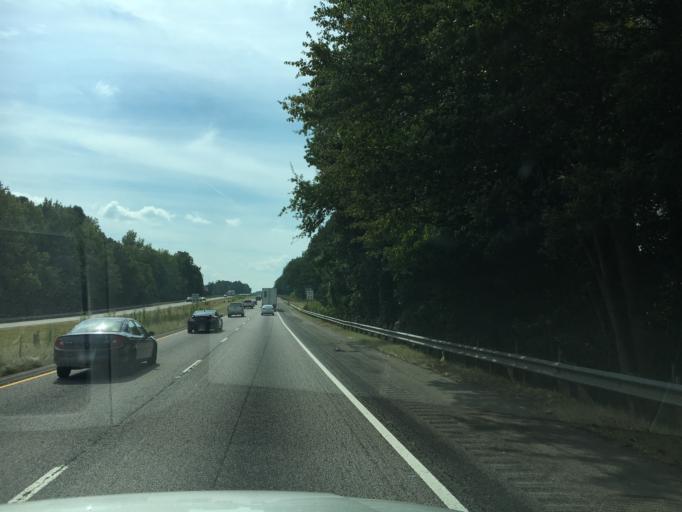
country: US
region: Georgia
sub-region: Gwinnett County
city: Dacula
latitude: 34.0770
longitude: -83.8938
